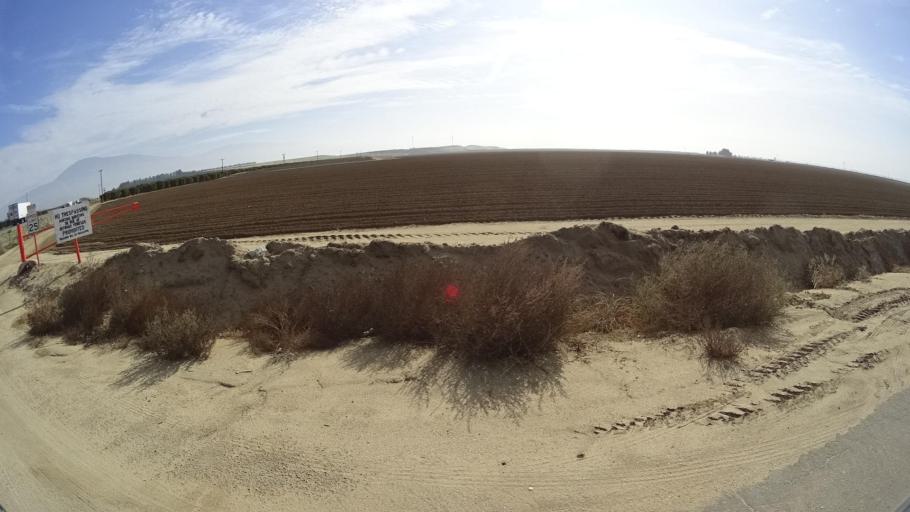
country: US
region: California
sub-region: Kern County
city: Arvin
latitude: 35.3258
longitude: -118.8001
